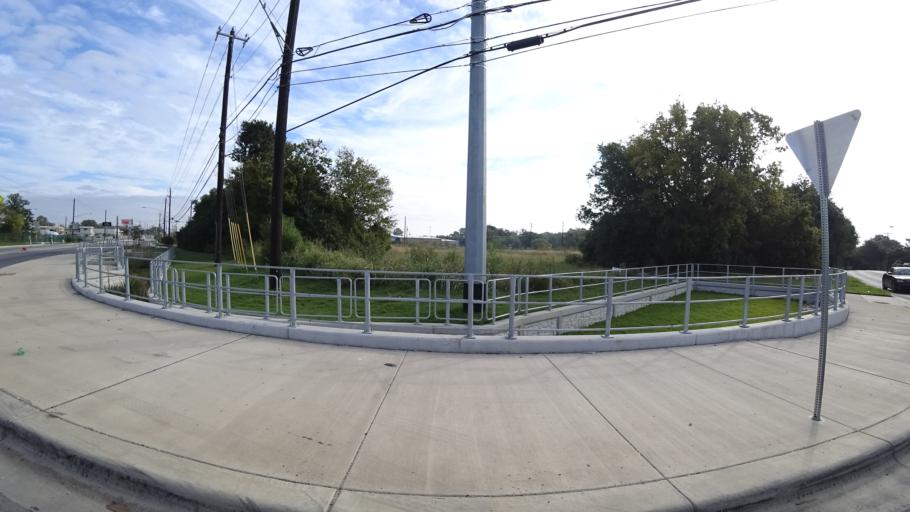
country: US
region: Texas
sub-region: Travis County
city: Austin
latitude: 30.2068
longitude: -97.7402
